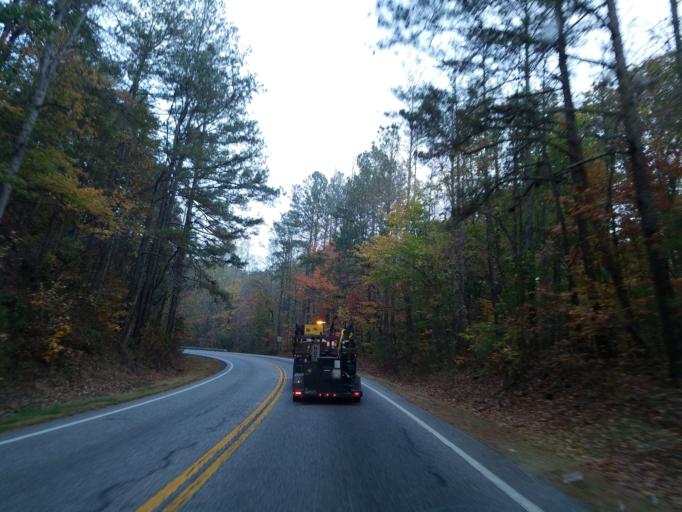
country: US
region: Georgia
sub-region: Gilmer County
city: Ellijay
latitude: 34.5801
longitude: -84.6399
